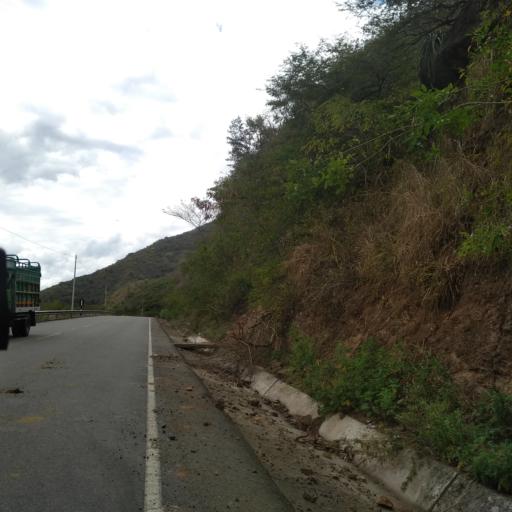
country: PE
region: Cajamarca
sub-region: Provincia de San Ignacio
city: Chirinos
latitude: -5.2339
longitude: -78.8675
